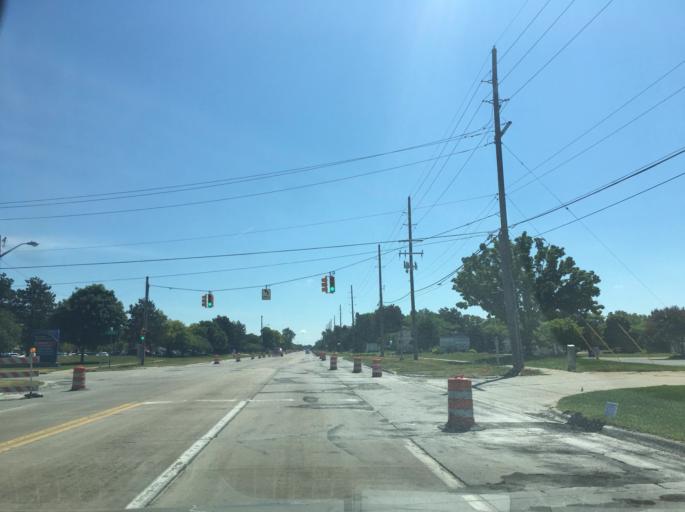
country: US
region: Michigan
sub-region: Macomb County
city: Clinton
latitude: 42.6127
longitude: -82.9634
